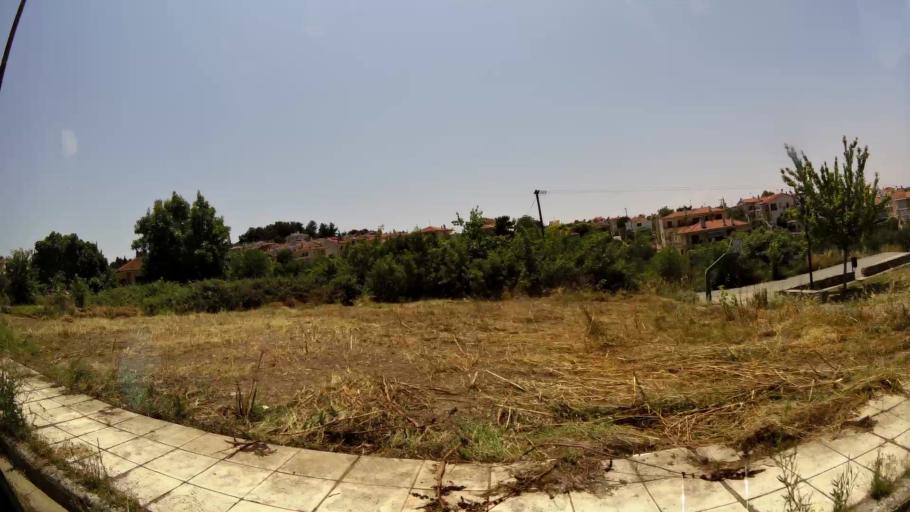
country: GR
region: Central Macedonia
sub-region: Nomos Thessalonikis
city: Trilofos
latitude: 40.4655
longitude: 22.9741
